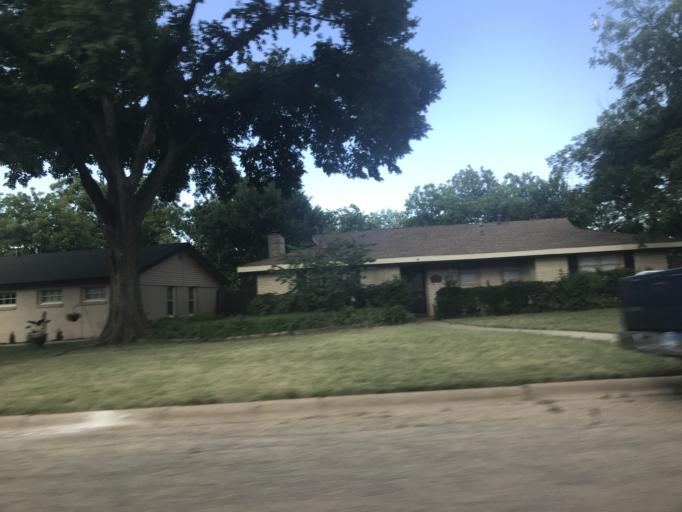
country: US
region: Texas
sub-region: Taylor County
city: Abilene
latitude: 32.4263
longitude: -99.7669
